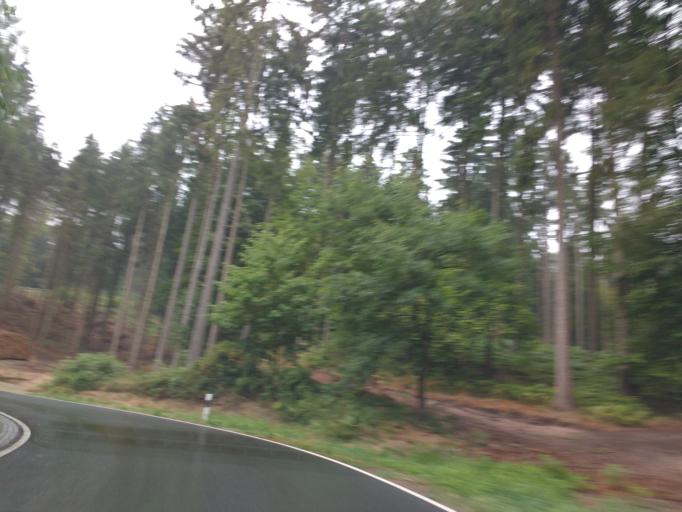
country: DE
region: Lower Saxony
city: Heyen
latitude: 52.0481
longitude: 9.5021
